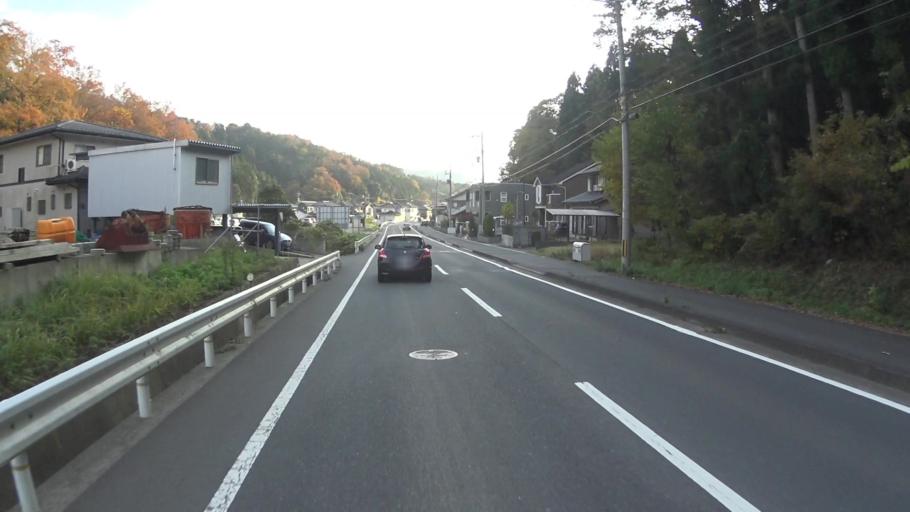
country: JP
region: Kyoto
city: Maizuru
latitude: 35.4896
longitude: 135.4367
